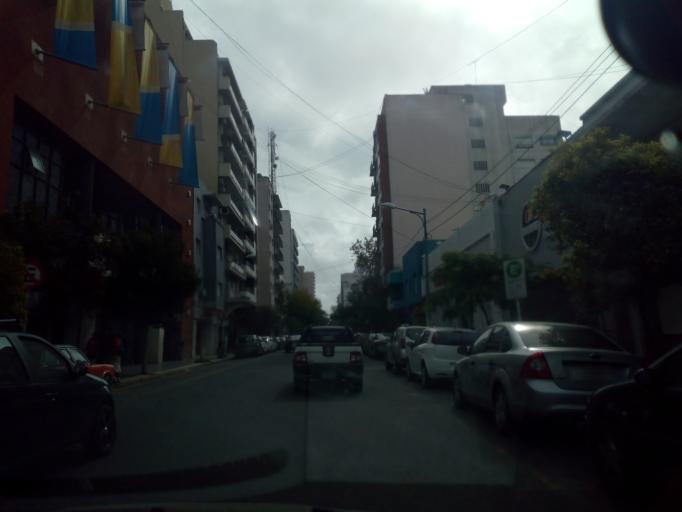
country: AR
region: Buenos Aires
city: Mar del Plata
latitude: -37.9981
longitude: -57.5515
